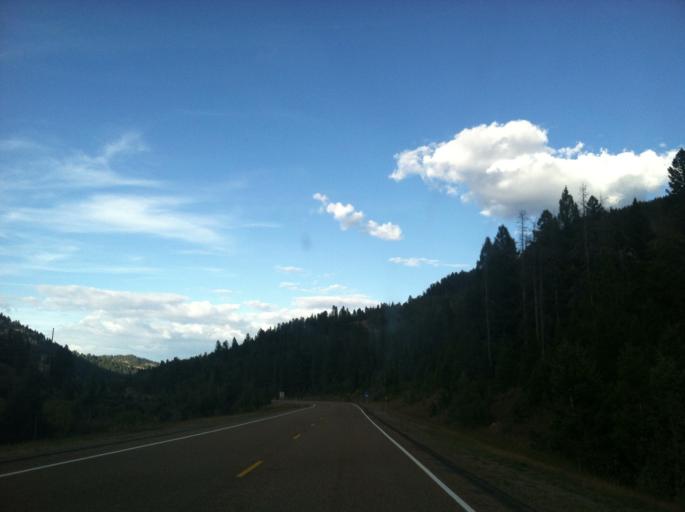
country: US
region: Montana
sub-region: Granite County
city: Philipsburg
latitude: 46.4229
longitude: -113.2776
